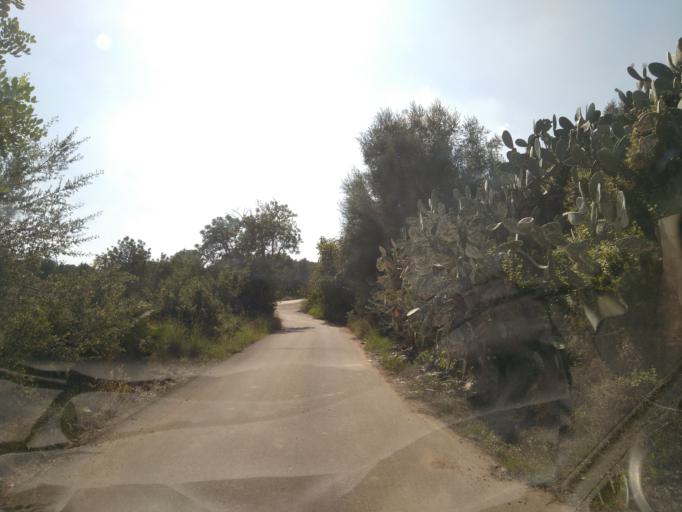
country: ES
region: Valencia
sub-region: Provincia de Valencia
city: Tous
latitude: 39.1794
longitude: -0.6017
